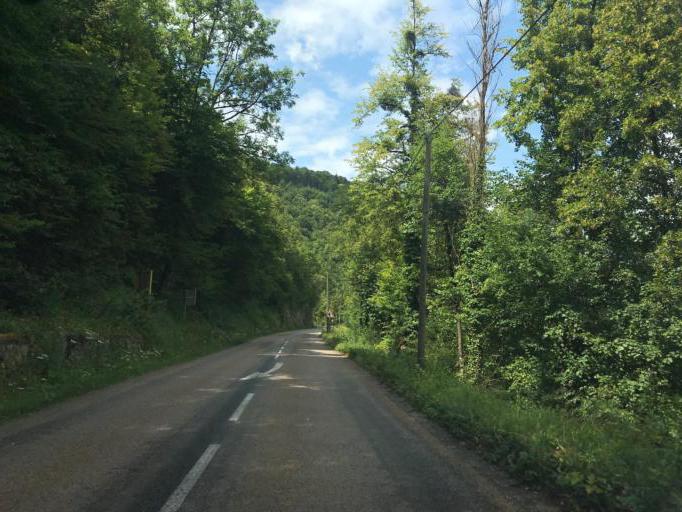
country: FR
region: Franche-Comte
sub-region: Departement du Jura
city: Saint-Claude
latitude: 46.4065
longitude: 5.8652
